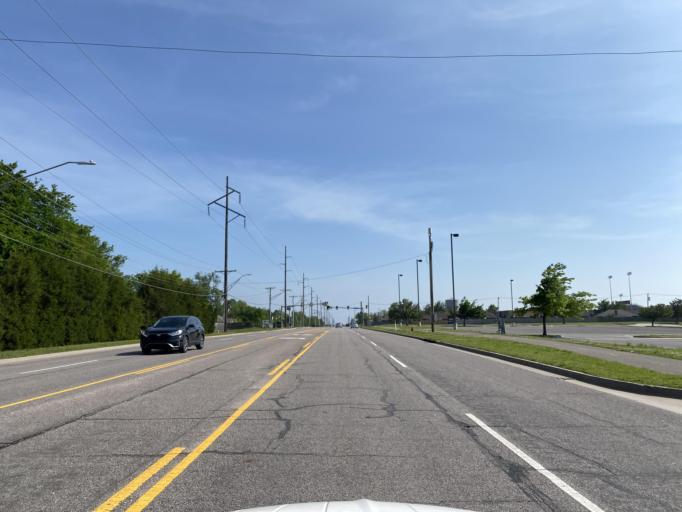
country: US
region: Oklahoma
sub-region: Oklahoma County
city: Midwest City
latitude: 35.4436
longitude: -97.3532
